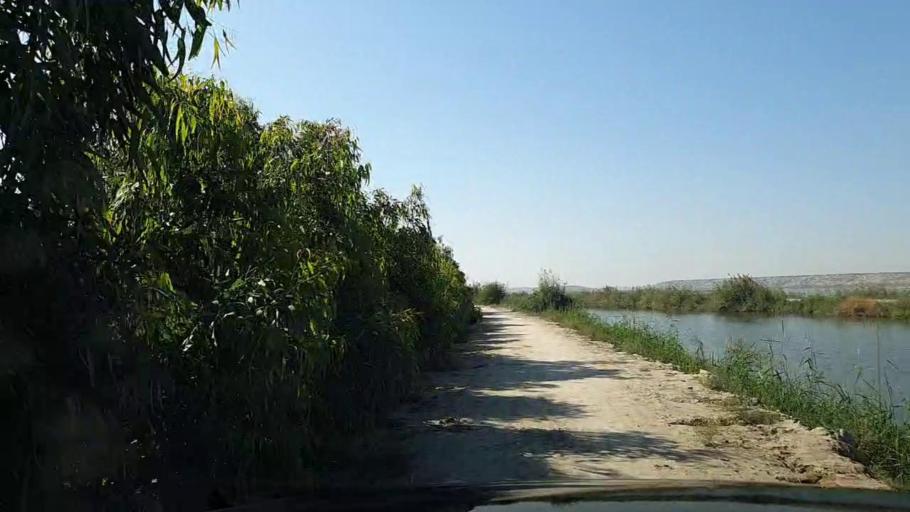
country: PK
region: Sindh
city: Thatta
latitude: 24.6952
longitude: 67.8958
